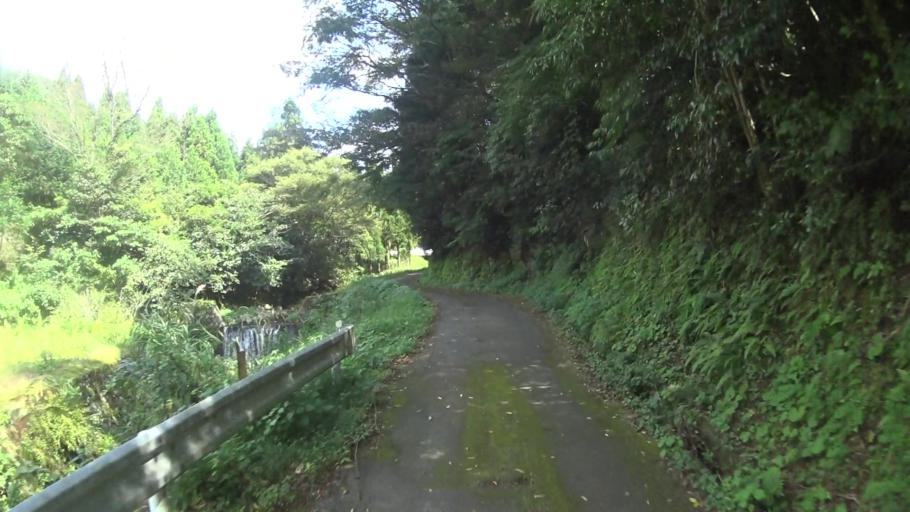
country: JP
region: Kyoto
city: Miyazu
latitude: 35.7426
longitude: 135.1862
